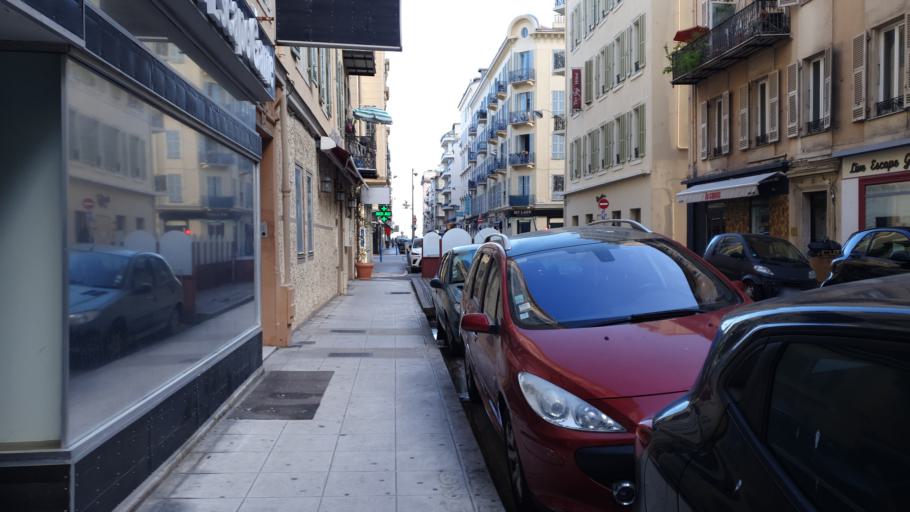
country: FR
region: Provence-Alpes-Cote d'Azur
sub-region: Departement des Alpes-Maritimes
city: Nice
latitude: 43.6973
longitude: 7.2605
